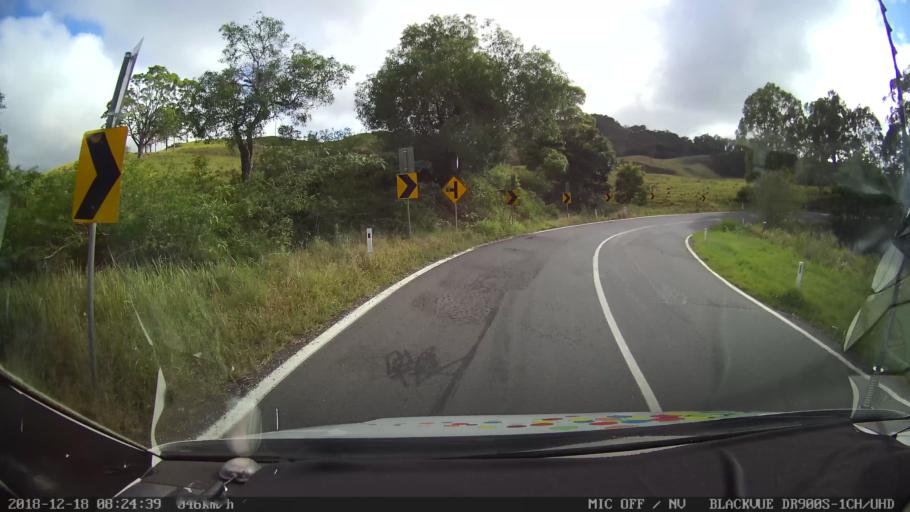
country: AU
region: New South Wales
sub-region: Kyogle
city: Kyogle
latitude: -28.3219
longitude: 152.7358
